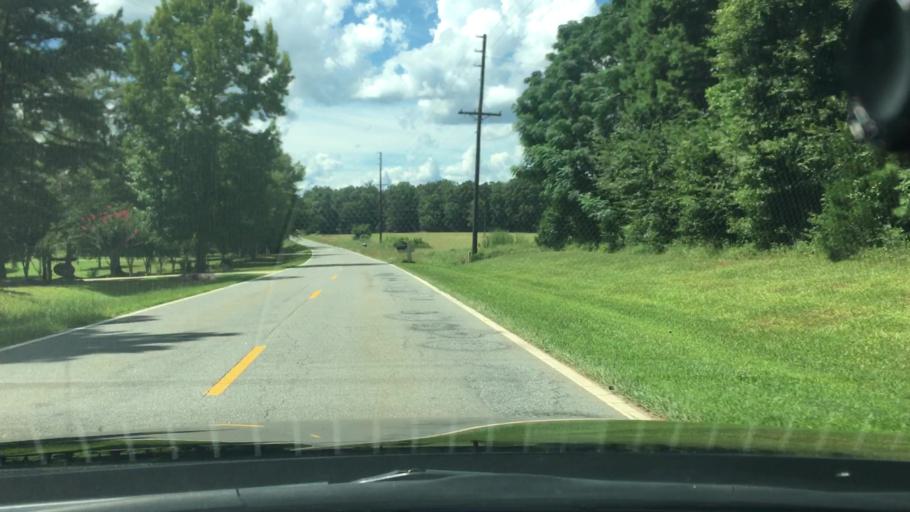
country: US
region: Georgia
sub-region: Putnam County
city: Jefferson
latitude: 33.3607
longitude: -83.2644
